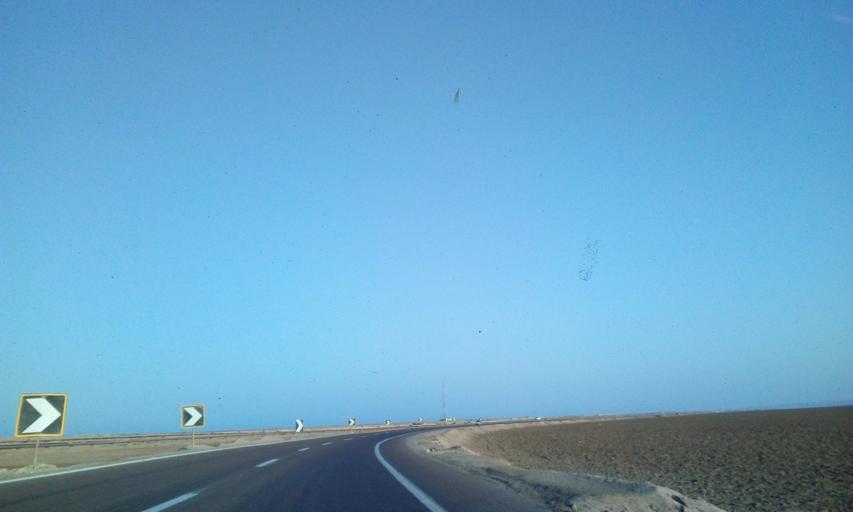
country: EG
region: South Sinai
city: Tor
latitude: 28.2689
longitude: 33.1482
